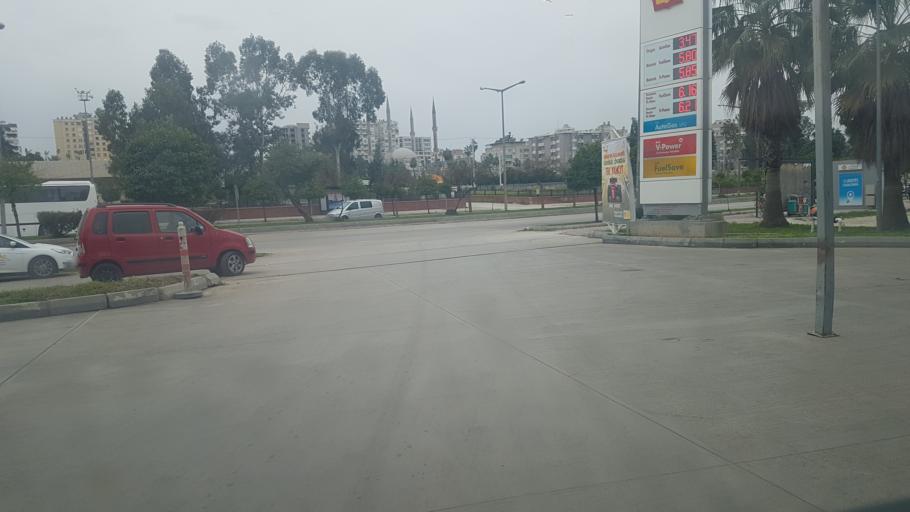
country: TR
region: Adana
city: Adana
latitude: 37.0055
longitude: 35.3176
